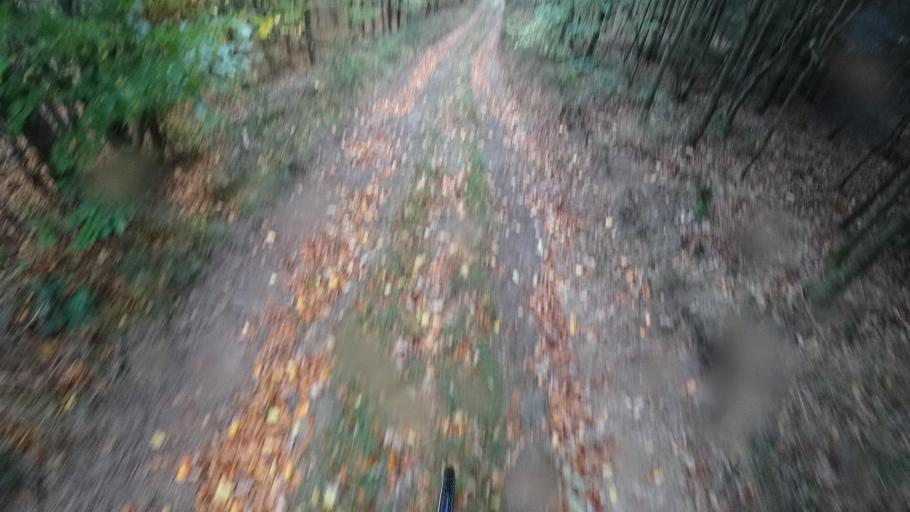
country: DE
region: Rheinland-Pfalz
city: Kirchsahr
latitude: 50.5234
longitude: 6.9086
